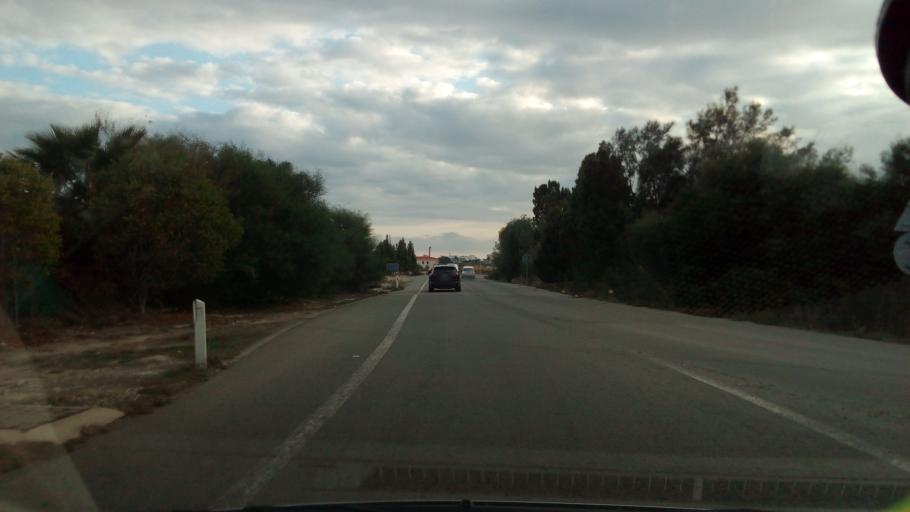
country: CY
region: Larnaka
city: Voroklini
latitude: 34.9724
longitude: 33.6574
